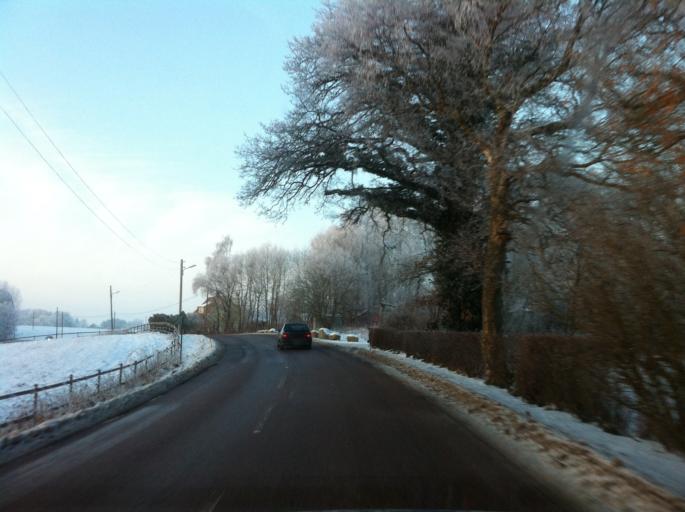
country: SE
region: Skane
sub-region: Svalovs Kommun
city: Kagerod
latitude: 56.0116
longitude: 13.0684
